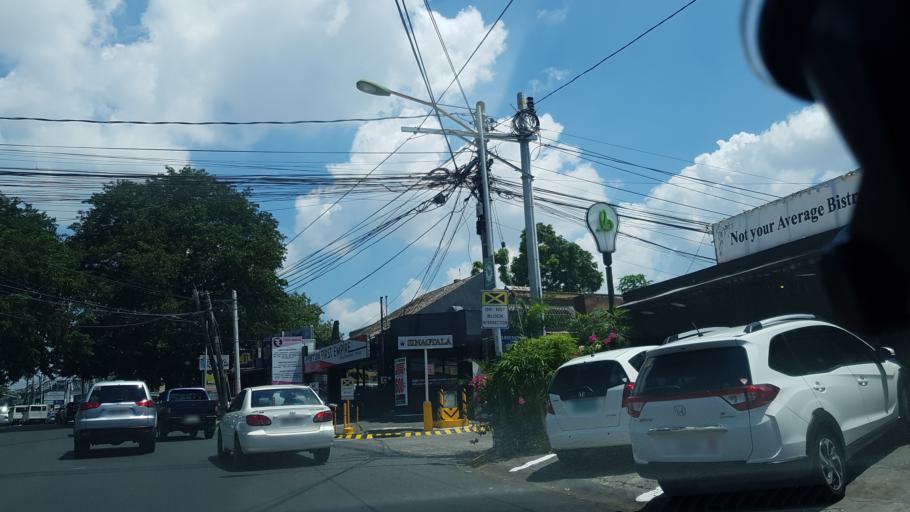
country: PH
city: Sambayanihan People's Village
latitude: 14.4450
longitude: 121.0239
